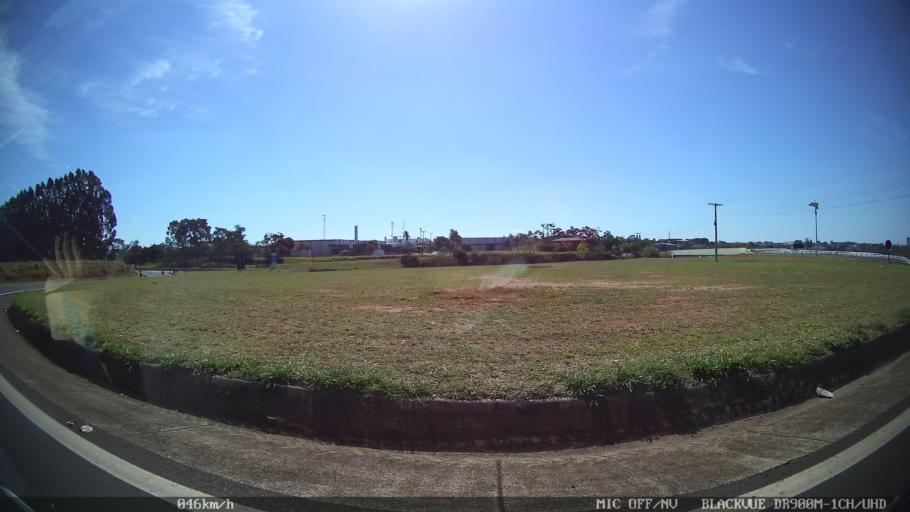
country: BR
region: Sao Paulo
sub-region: Franca
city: Franca
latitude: -20.5587
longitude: -47.4412
